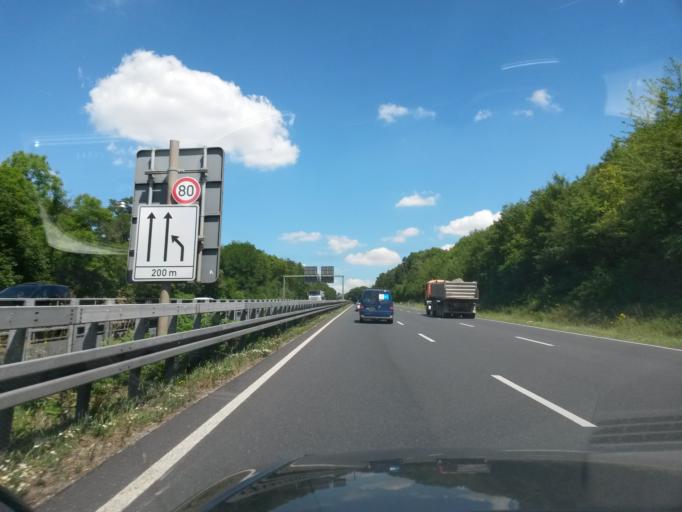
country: DE
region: Bavaria
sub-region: Regierungsbezirk Unterfranken
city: Wuerzburg
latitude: 49.8038
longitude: 9.9642
